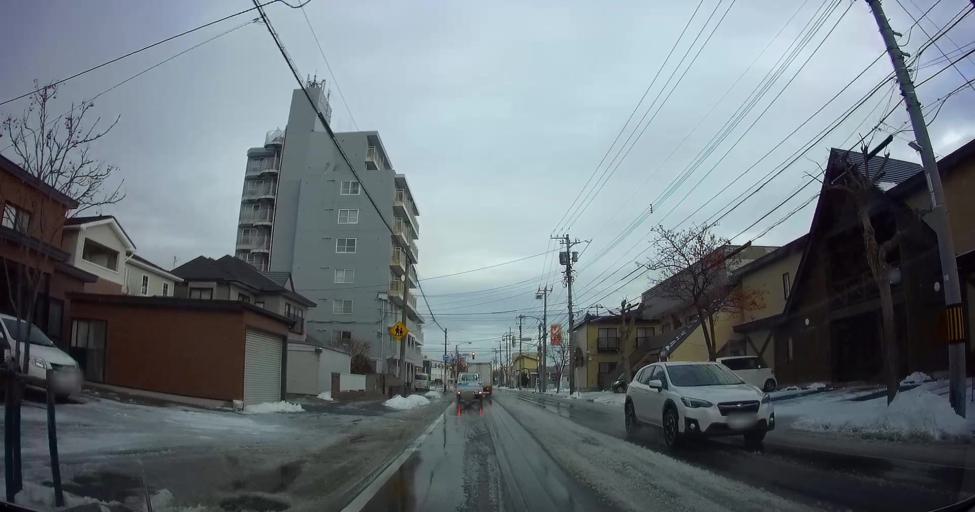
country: JP
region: Hokkaido
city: Hakodate
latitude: 41.7785
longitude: 140.7533
